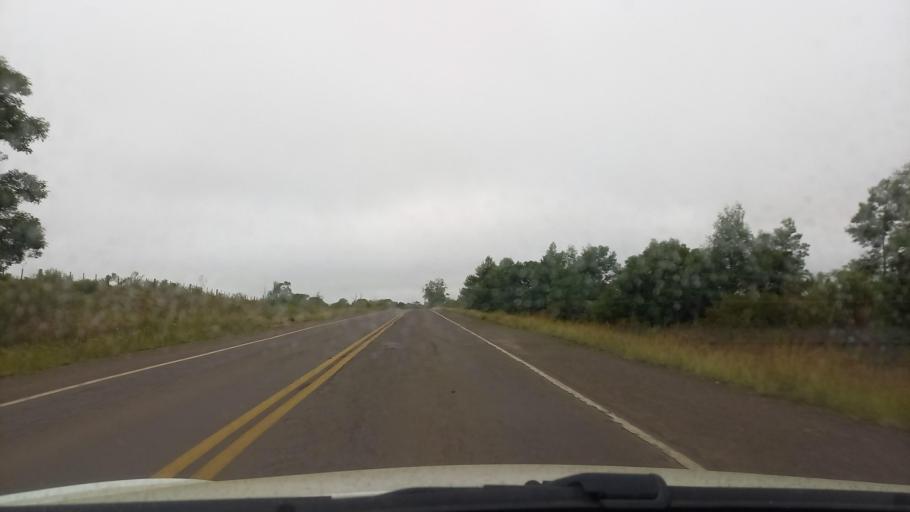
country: BR
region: Rio Grande do Sul
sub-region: Cacequi
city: Cacequi
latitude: -30.0922
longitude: -54.6291
